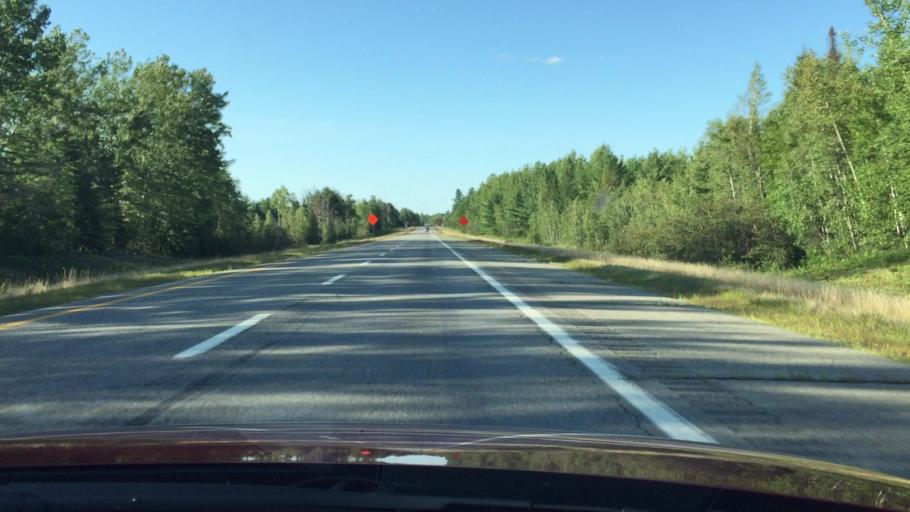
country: US
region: Maine
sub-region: Penobscot County
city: Howland
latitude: 45.2529
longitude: -68.6791
